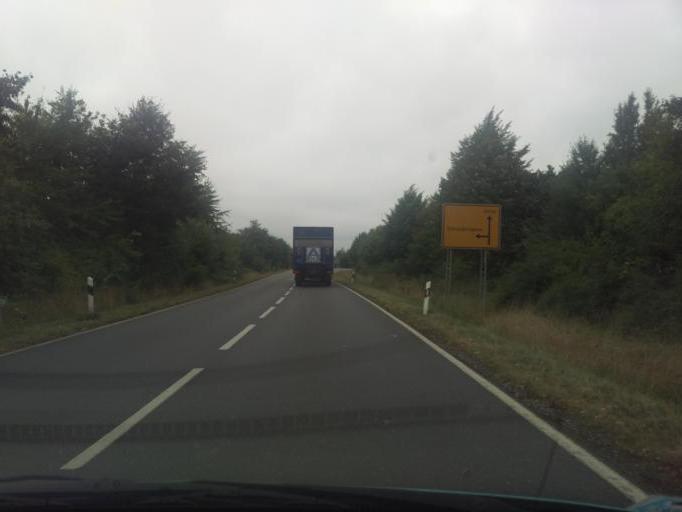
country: DE
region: Lower Saxony
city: Dollbergen
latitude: 52.4047
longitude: 10.1729
